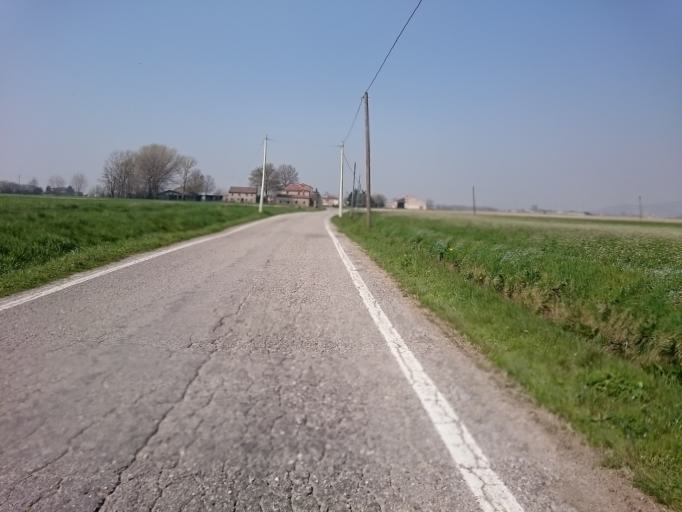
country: IT
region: Veneto
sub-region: Provincia di Padova
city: Villa Estense
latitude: 45.1948
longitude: 11.6701
